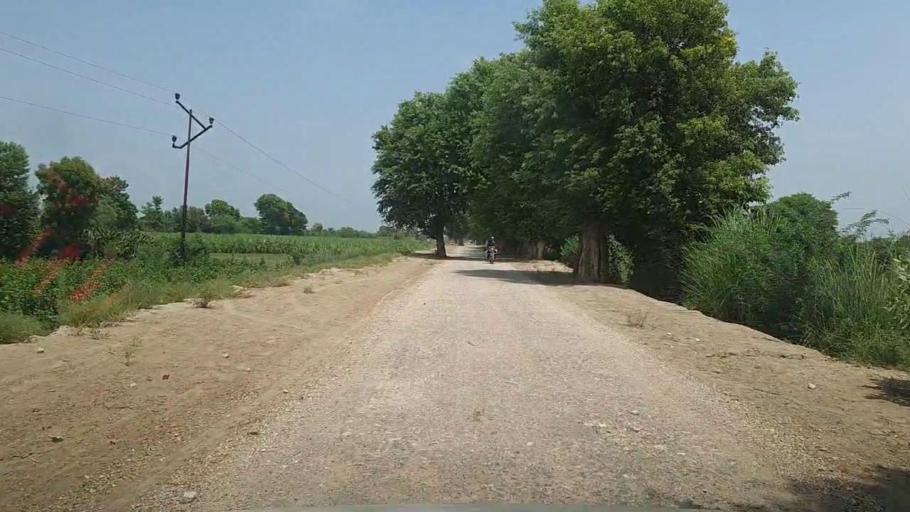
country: PK
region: Sindh
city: Karaundi
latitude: 26.9135
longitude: 68.3367
